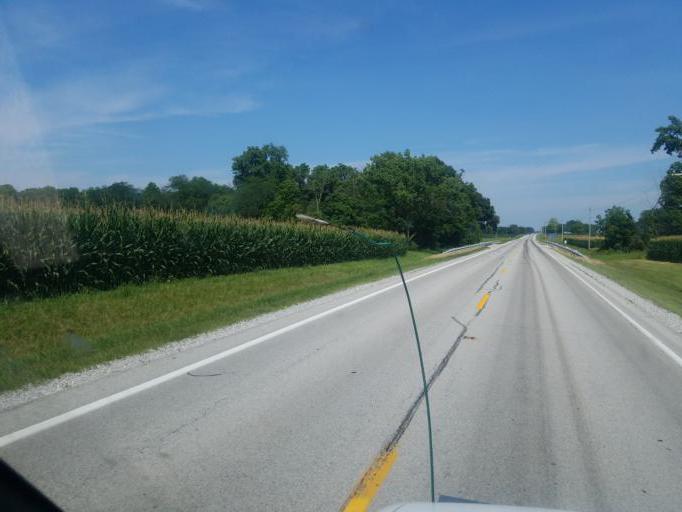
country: US
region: Ohio
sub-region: Shelby County
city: Botkins
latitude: 40.4963
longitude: -84.2816
